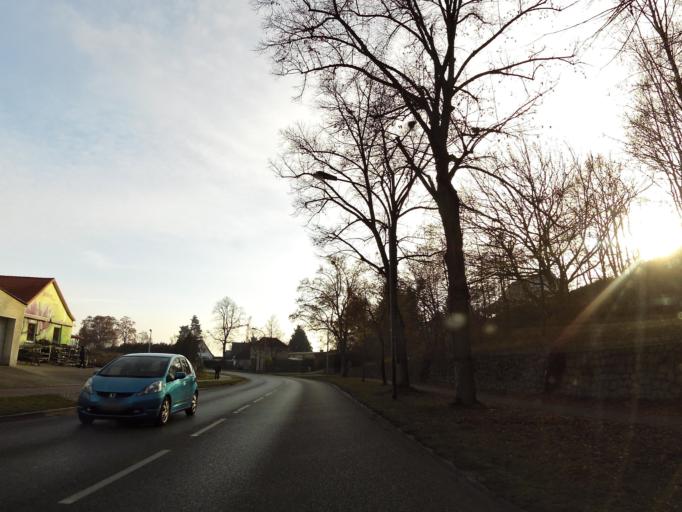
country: DE
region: Brandenburg
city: Werder
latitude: 52.3674
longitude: 12.9297
